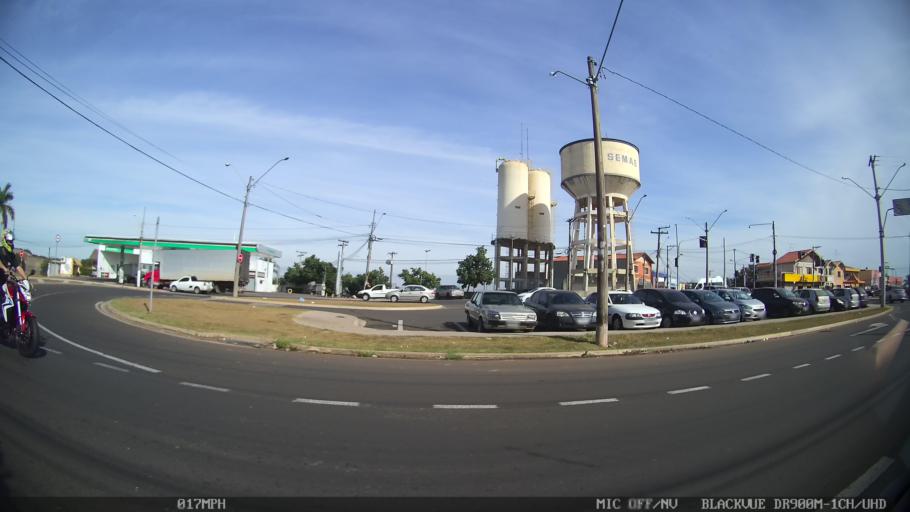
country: BR
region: Sao Paulo
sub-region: Piracicaba
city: Piracicaba
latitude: -22.7538
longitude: -47.6474
